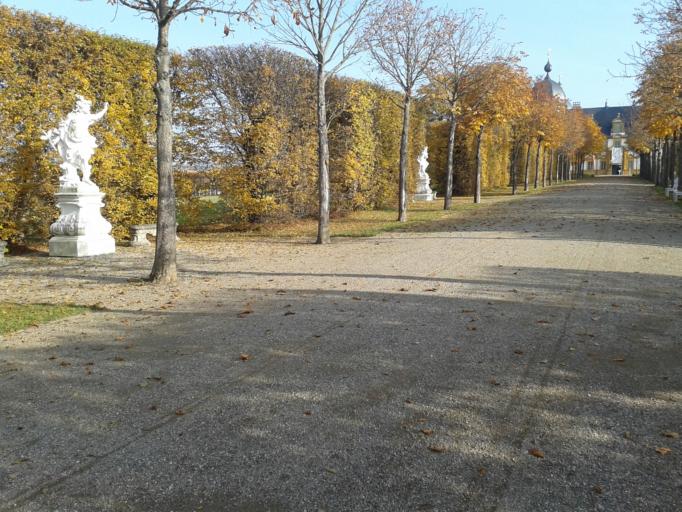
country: DE
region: Bavaria
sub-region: Upper Franconia
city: Memmelsdorf
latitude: 49.9279
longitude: 10.9447
